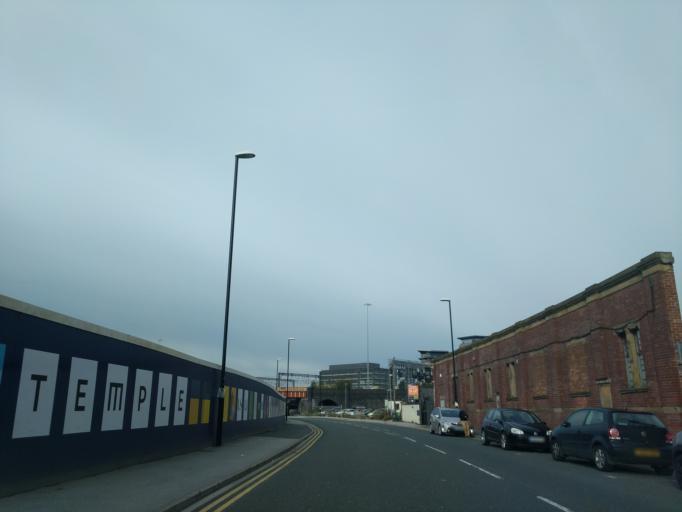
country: GB
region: England
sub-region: City and Borough of Leeds
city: Leeds
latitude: 53.7923
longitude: -1.5530
